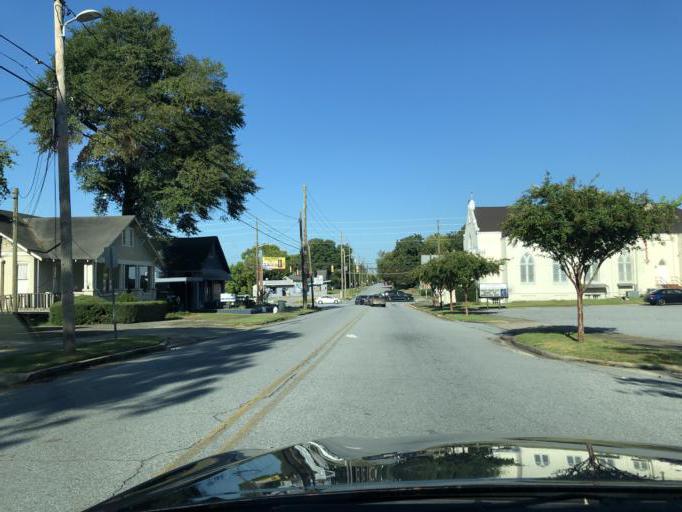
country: US
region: Georgia
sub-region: Muscogee County
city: Columbus
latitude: 32.4784
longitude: -84.9733
